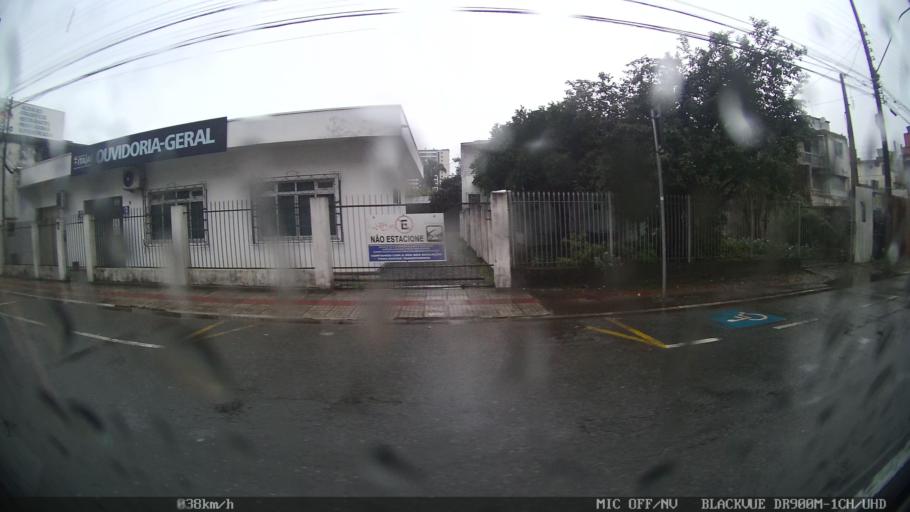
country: BR
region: Santa Catarina
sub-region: Itajai
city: Itajai
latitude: -26.9038
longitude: -48.6691
